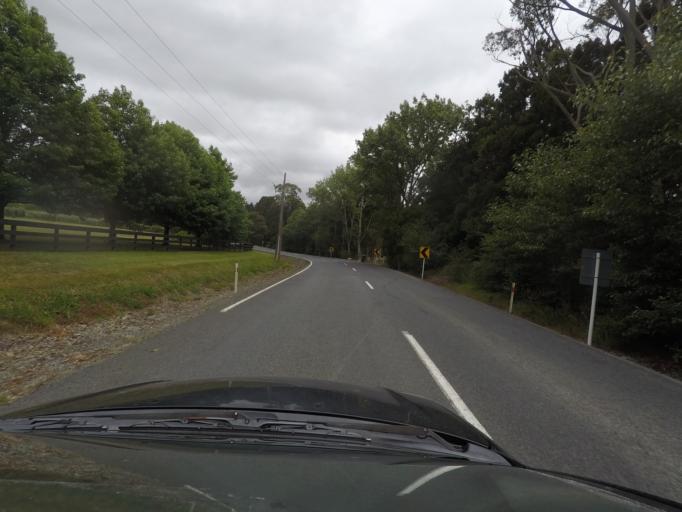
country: NZ
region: Auckland
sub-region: Auckland
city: Wellsford
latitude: -36.2837
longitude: 174.6110
